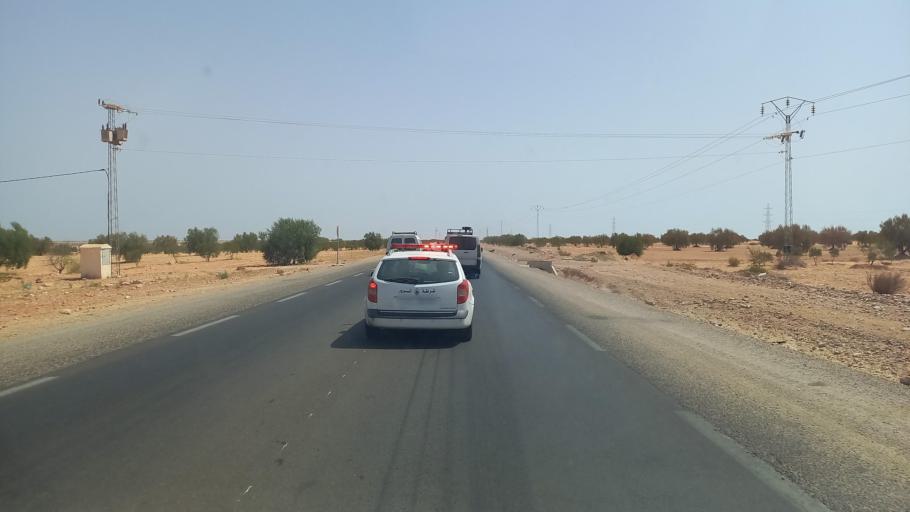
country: TN
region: Madanin
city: Zarzis
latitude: 33.3989
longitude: 10.8307
